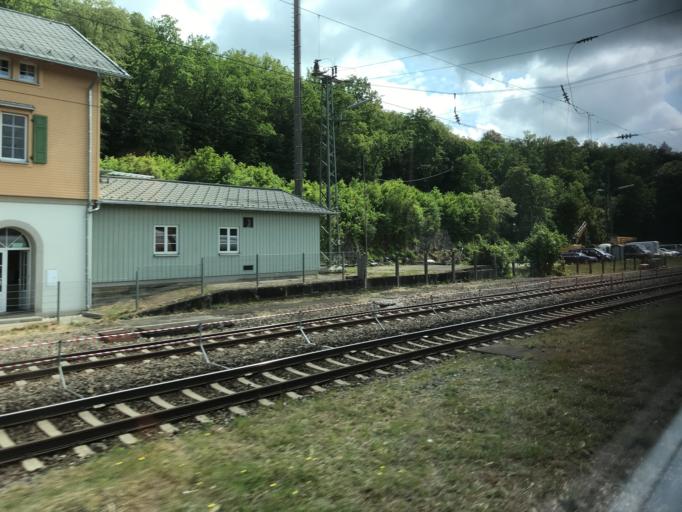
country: DE
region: Baden-Wuerttemberg
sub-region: Tuebingen Region
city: Westerstetten
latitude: 48.5252
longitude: 9.9432
